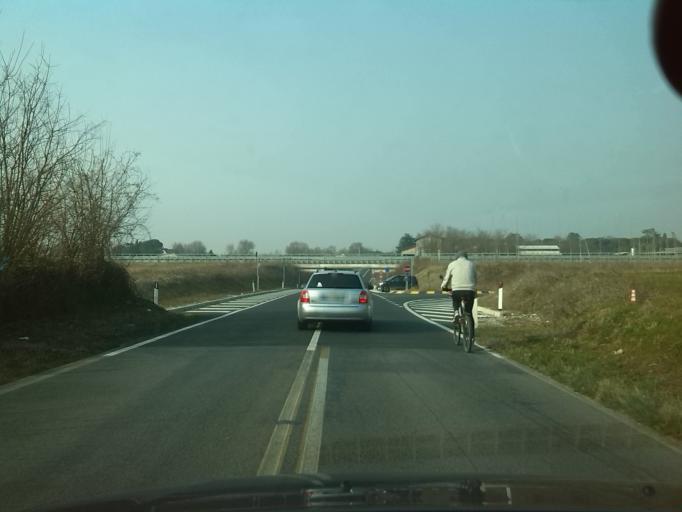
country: IT
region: Friuli Venezia Giulia
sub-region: Provincia di Gorizia
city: Gradisca d'Isonzo
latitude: 45.9001
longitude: 13.4975
